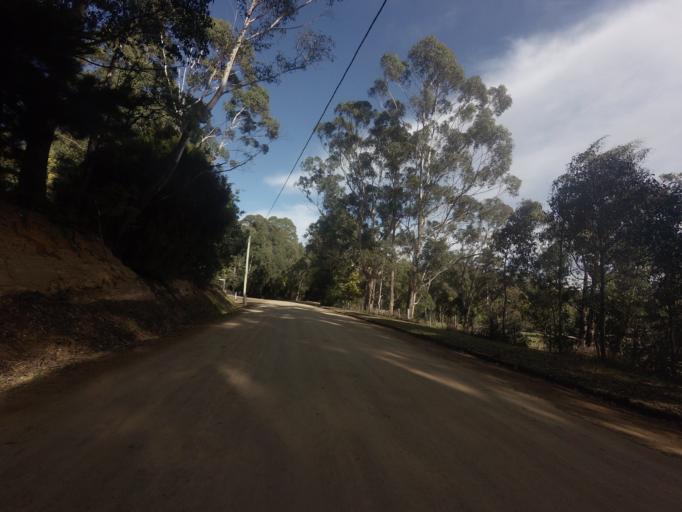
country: AU
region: Tasmania
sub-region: Huon Valley
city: Huonville
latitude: -43.0749
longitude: 147.0753
